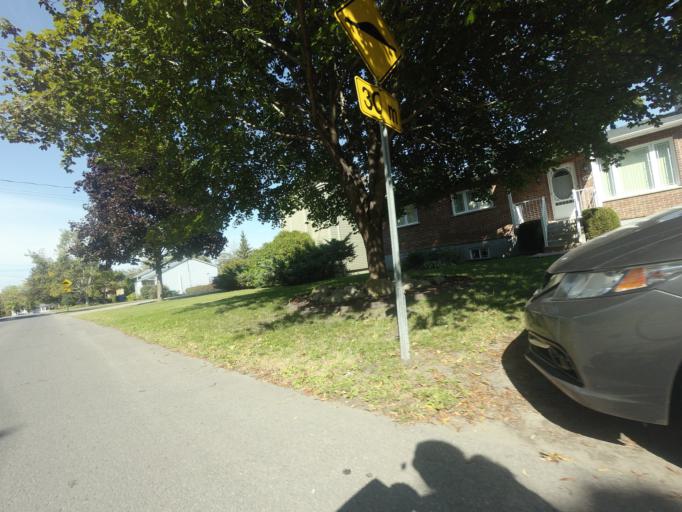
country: CA
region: Quebec
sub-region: Laurentides
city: Saint-Eustache
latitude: 45.5563
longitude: -73.9084
